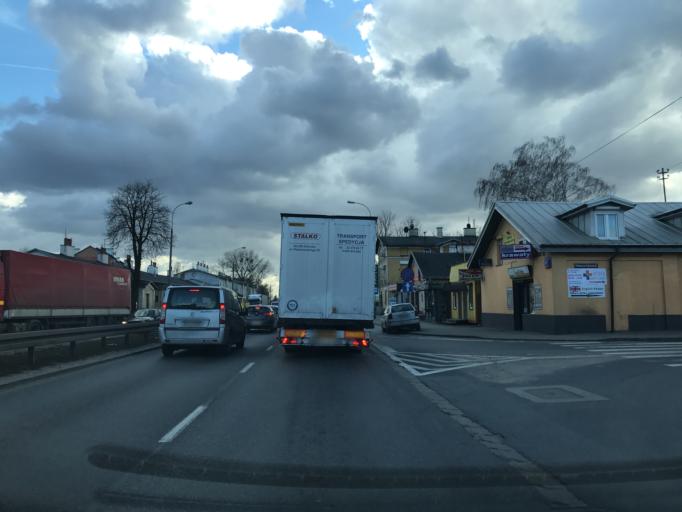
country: PL
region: Masovian Voivodeship
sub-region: Powiat wolominski
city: Marki
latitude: 52.3206
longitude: 21.1029
